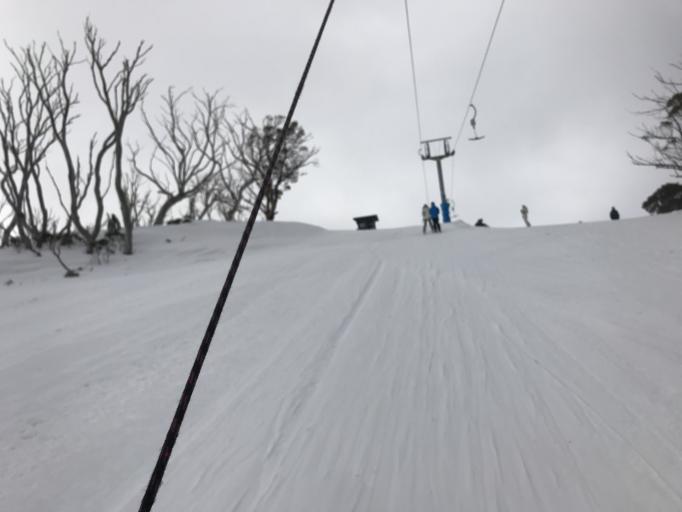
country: AU
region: New South Wales
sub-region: Snowy River
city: Jindabyne
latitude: -36.3831
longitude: 148.3773
